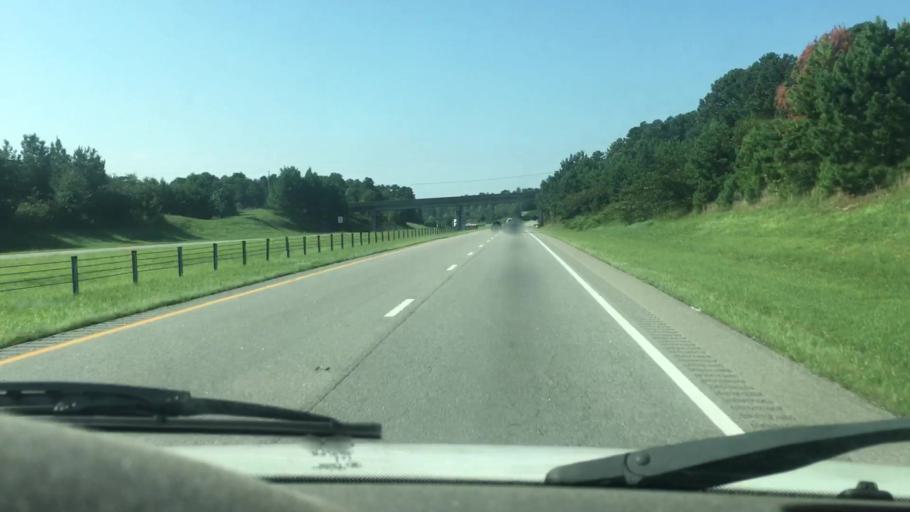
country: US
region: North Carolina
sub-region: Lincoln County
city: Lowesville
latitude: 35.3903
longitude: -80.9992
